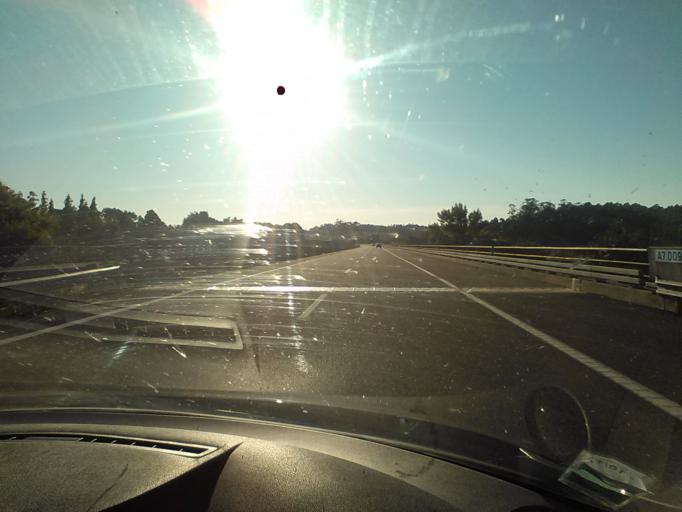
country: PT
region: Porto
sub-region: Vila do Conde
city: Arvore
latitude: 41.3924
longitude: -8.6775
